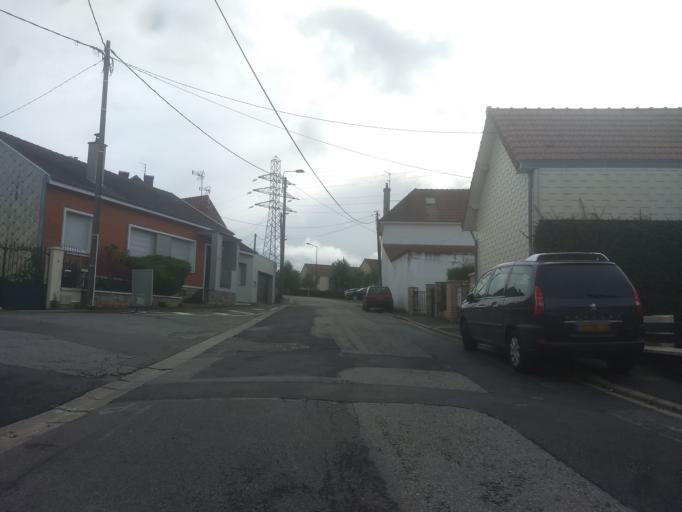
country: FR
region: Nord-Pas-de-Calais
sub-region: Departement du Pas-de-Calais
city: Anzin-Saint-Aubin
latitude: 50.3071
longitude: 2.7541
